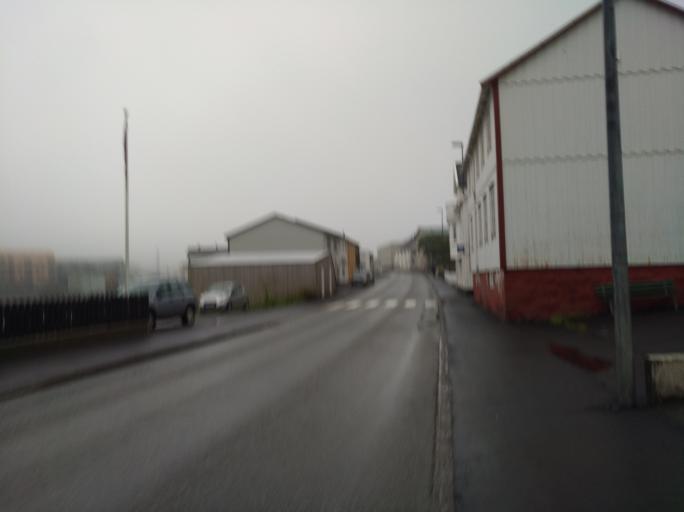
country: FO
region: Nordoyar
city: Klaksvik
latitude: 62.2274
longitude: -6.5911
